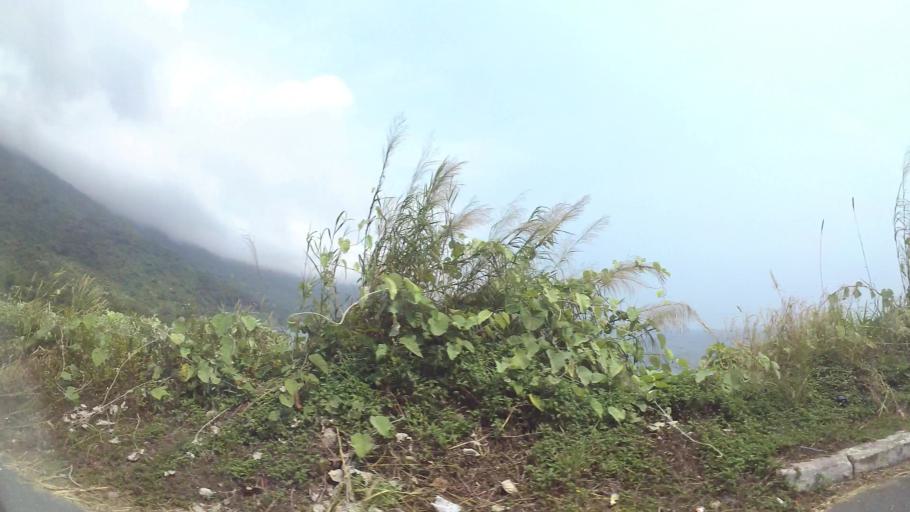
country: VN
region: Da Nang
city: Son Tra
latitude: 16.1002
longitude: 108.2812
